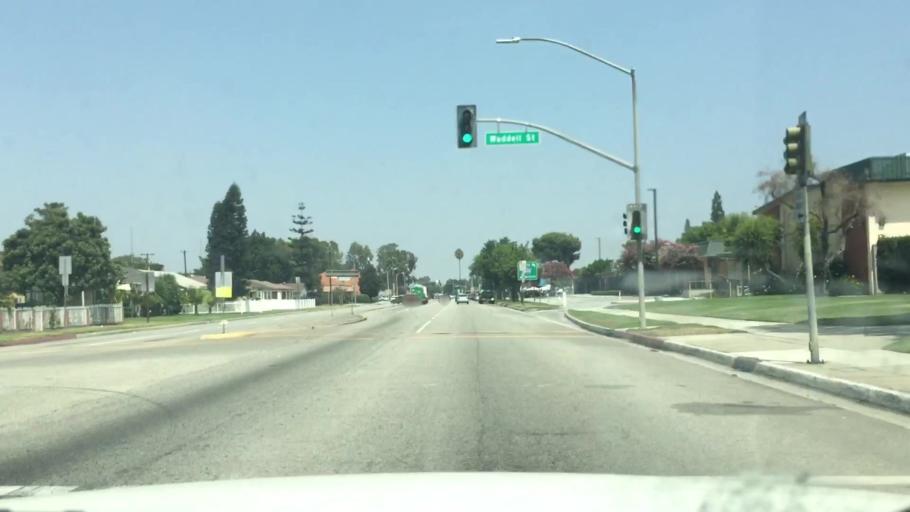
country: US
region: California
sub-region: Los Angeles County
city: West Whittier-Los Nietos
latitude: 33.9701
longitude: -118.0807
